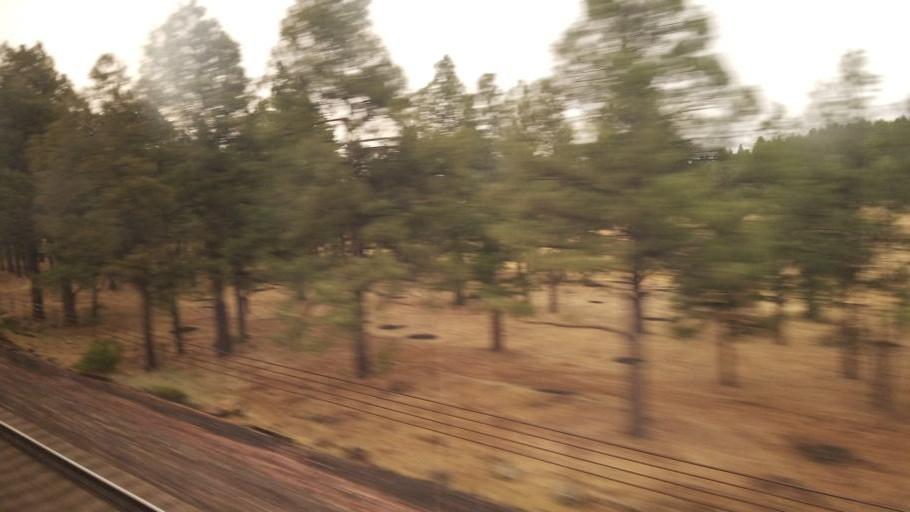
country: US
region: Arizona
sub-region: Coconino County
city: Parks
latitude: 35.2348
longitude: -112.0047
